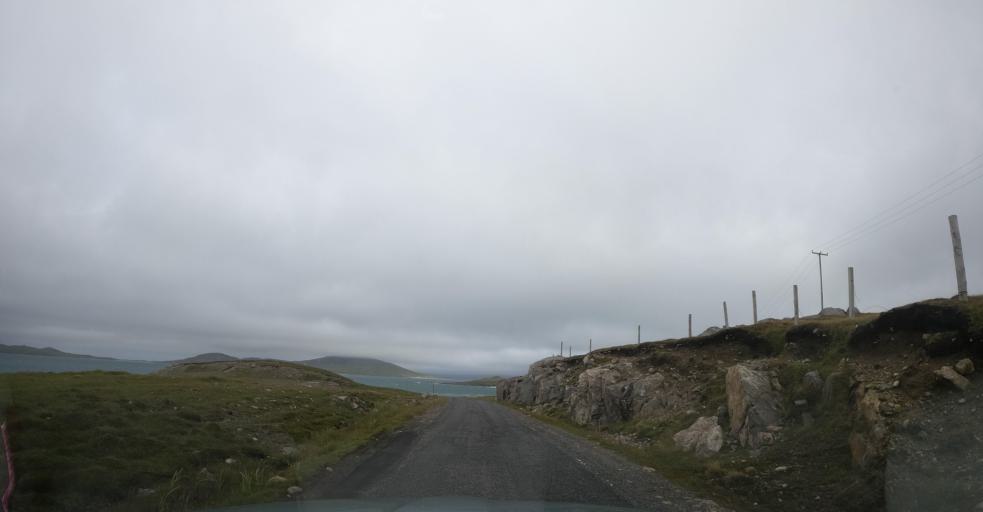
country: GB
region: Scotland
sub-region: Eilean Siar
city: Harris
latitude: 57.8559
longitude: -6.9983
